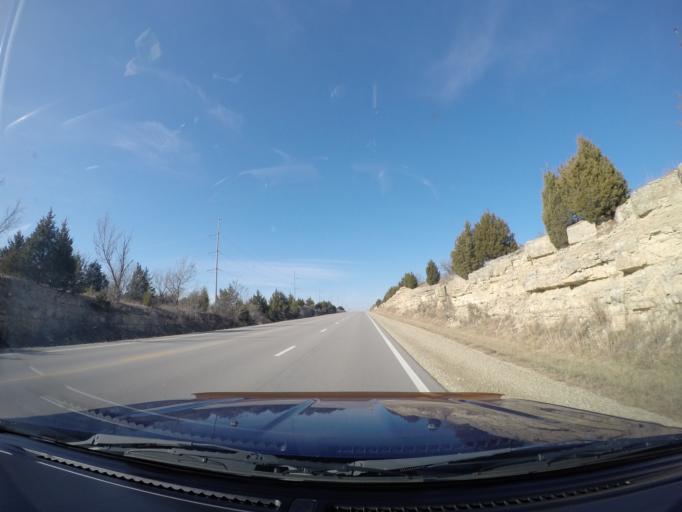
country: US
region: Kansas
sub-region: Riley County
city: Manhattan
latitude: 39.2519
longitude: -96.6465
